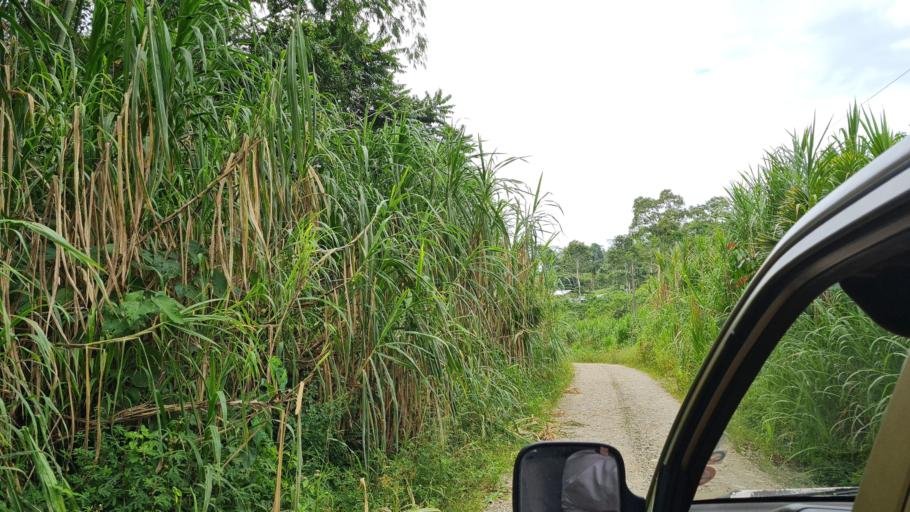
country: EC
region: Napo
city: Tena
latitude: -0.9934
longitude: -77.7490
